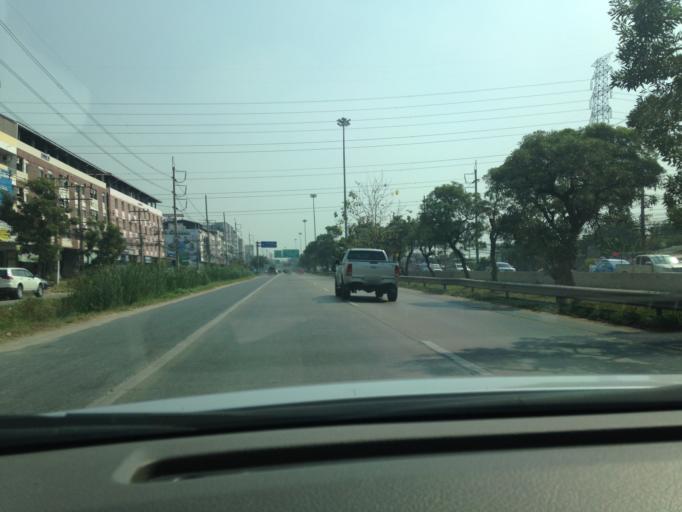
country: TH
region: Pathum Thani
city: Khlong Luang
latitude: 14.0654
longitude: 100.6081
